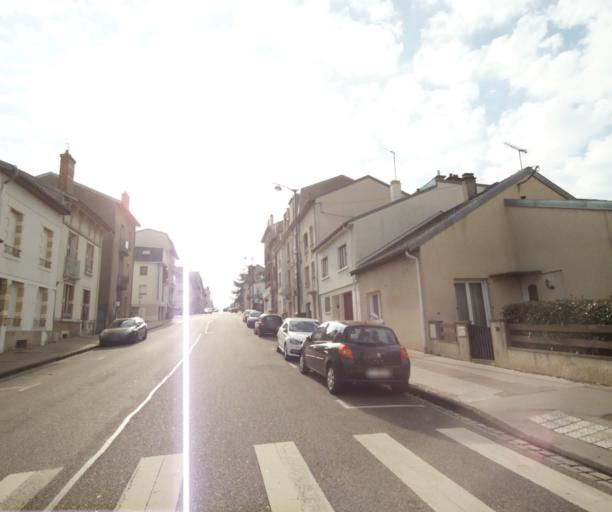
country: FR
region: Lorraine
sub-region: Departement de Meurthe-et-Moselle
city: Laxou
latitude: 48.6815
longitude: 6.1566
